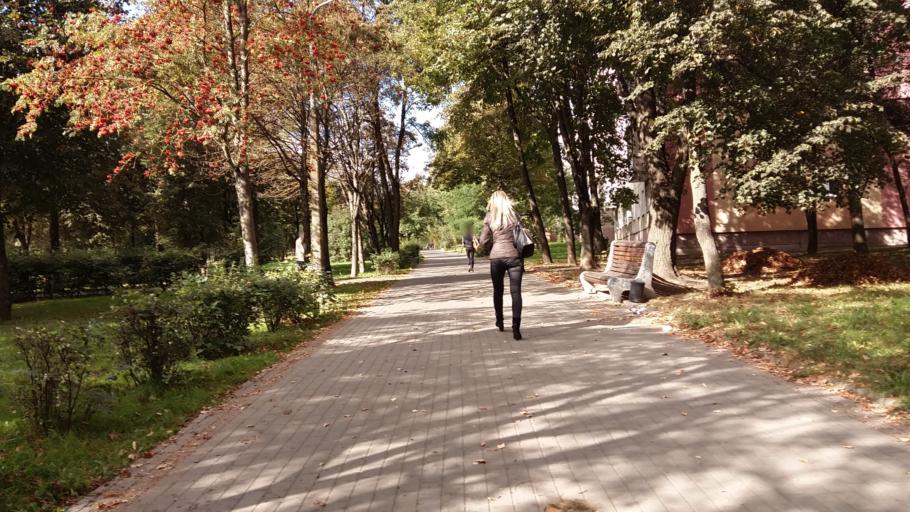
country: BY
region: Grodnenskaya
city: Hrodna
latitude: 53.6982
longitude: 23.8006
